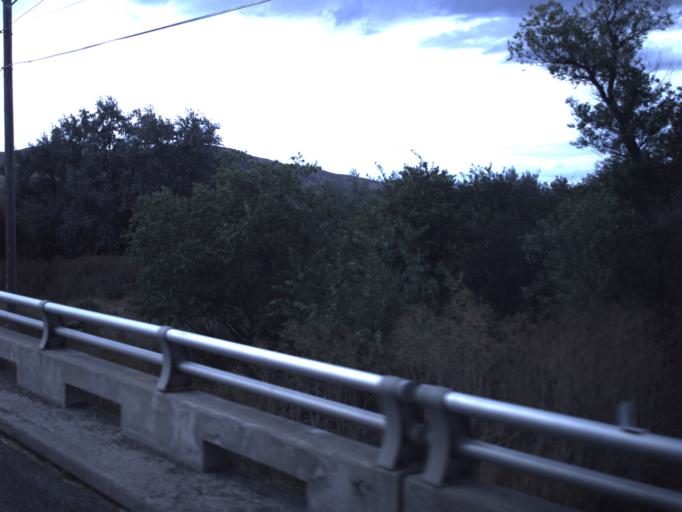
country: US
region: Utah
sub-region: Cache County
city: Lewiston
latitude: 41.9754
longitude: -111.9372
